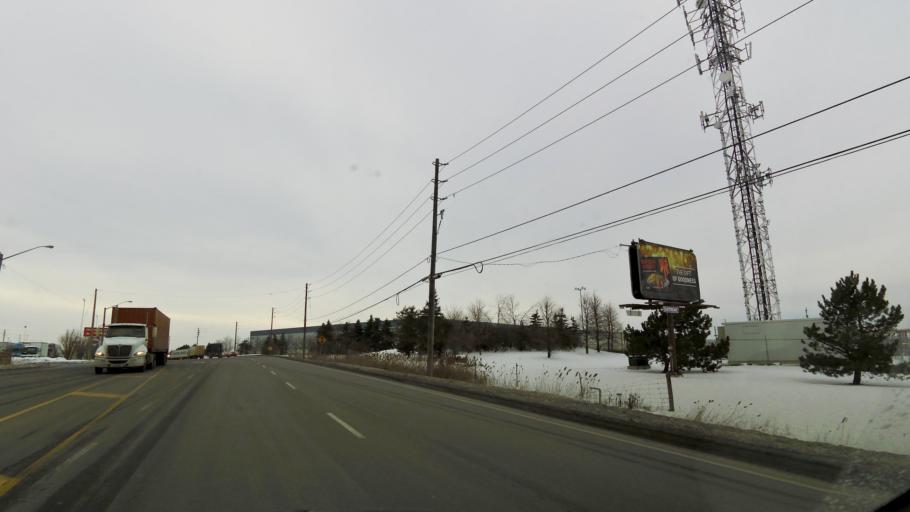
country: CA
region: Ontario
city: Brampton
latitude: 43.8034
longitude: -79.6652
